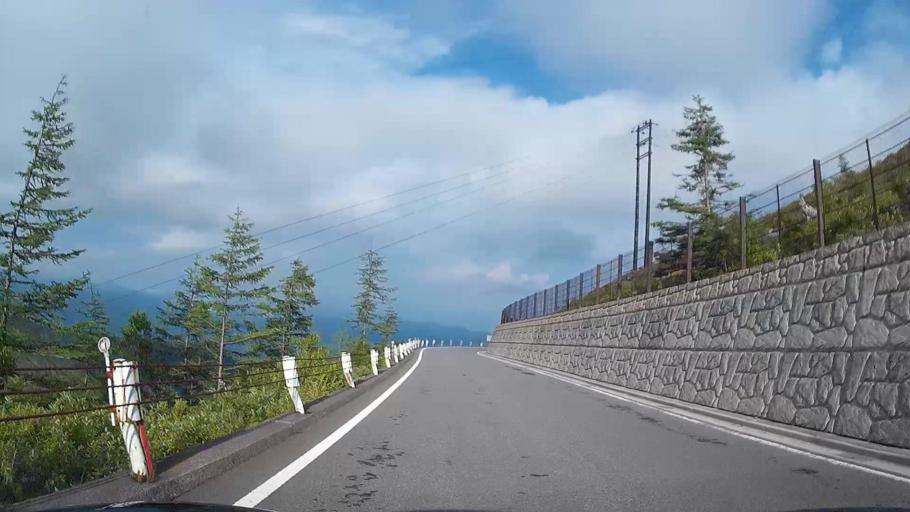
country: JP
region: Nagano
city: Nakano
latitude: 36.6346
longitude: 138.5470
